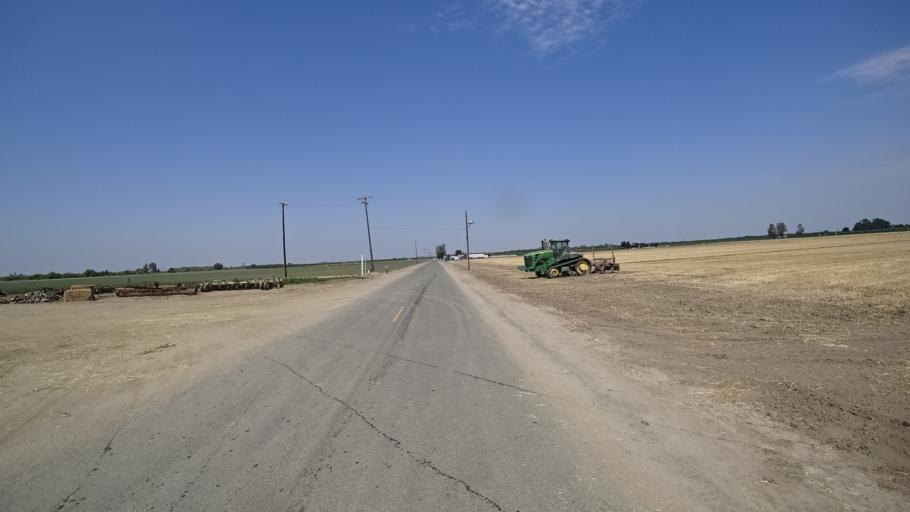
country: US
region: California
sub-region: Fresno County
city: Riverdale
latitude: 36.3948
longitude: -119.7932
